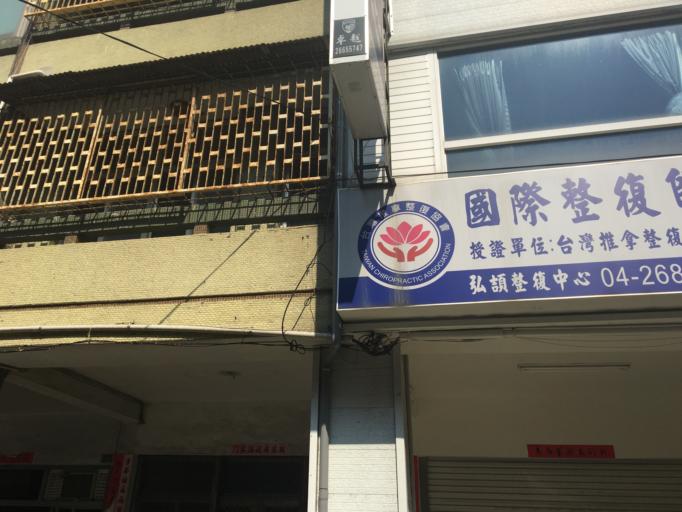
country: TW
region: Taiwan
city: Fengyuan
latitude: 24.3411
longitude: 120.6237
